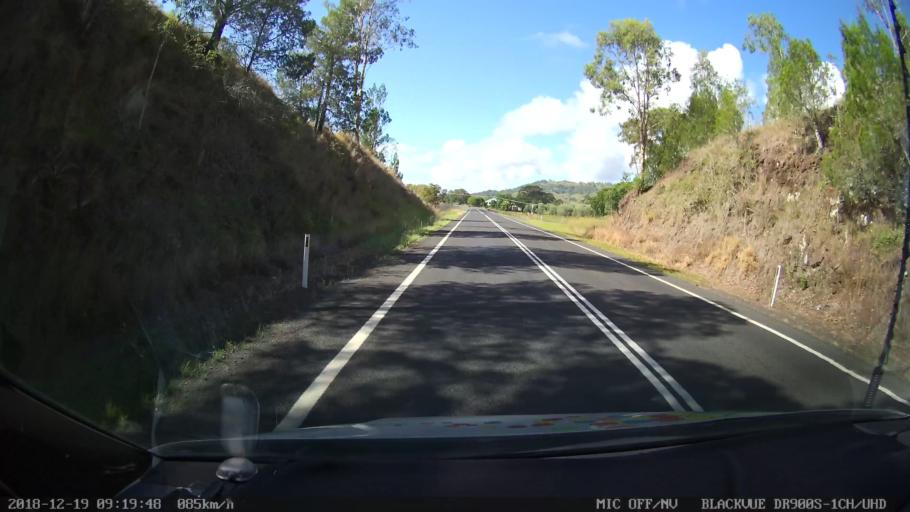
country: AU
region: New South Wales
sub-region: Kyogle
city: Kyogle
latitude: -28.5645
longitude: 152.9782
